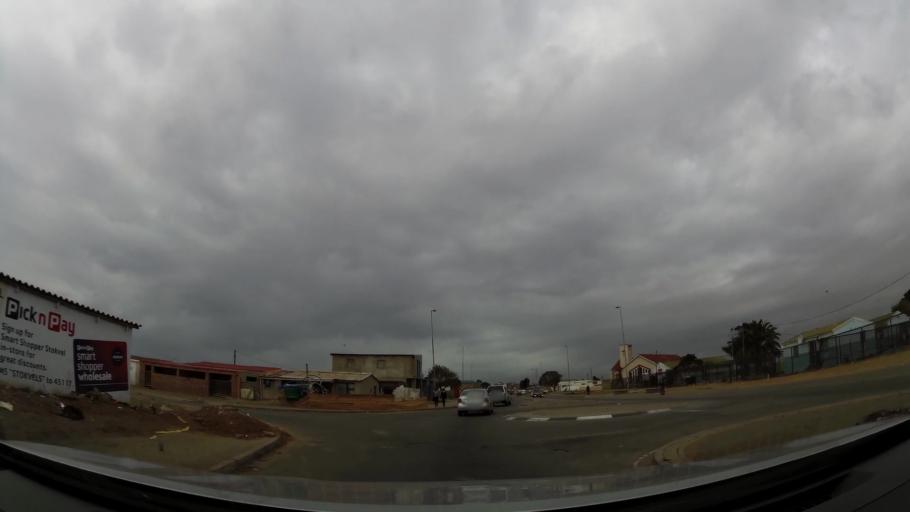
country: ZA
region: Eastern Cape
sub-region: Nelson Mandela Bay Metropolitan Municipality
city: Port Elizabeth
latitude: -33.8876
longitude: 25.5862
